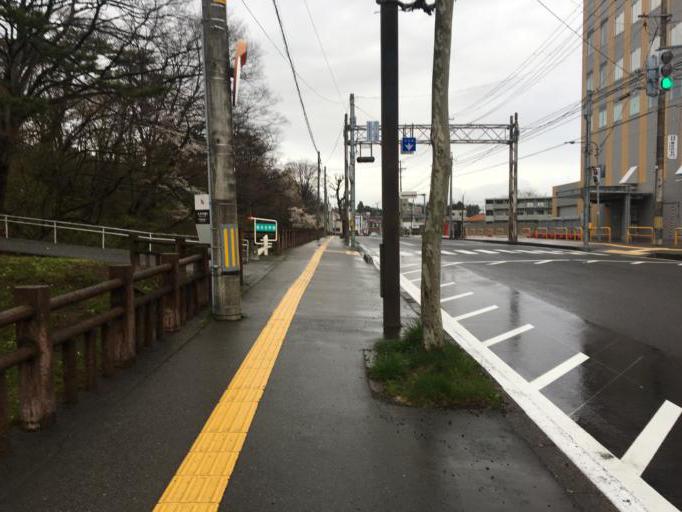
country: JP
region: Akita
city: Akita
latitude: 39.7200
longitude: 140.1255
